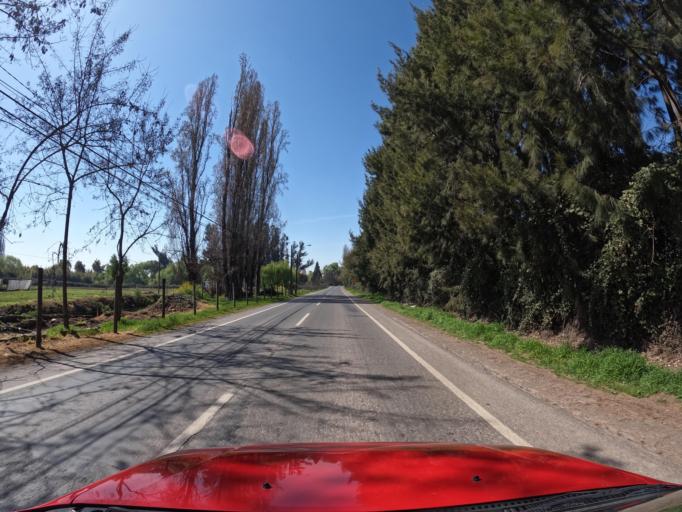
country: CL
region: Maule
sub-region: Provincia de Curico
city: Rauco
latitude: -34.9950
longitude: -71.3535
